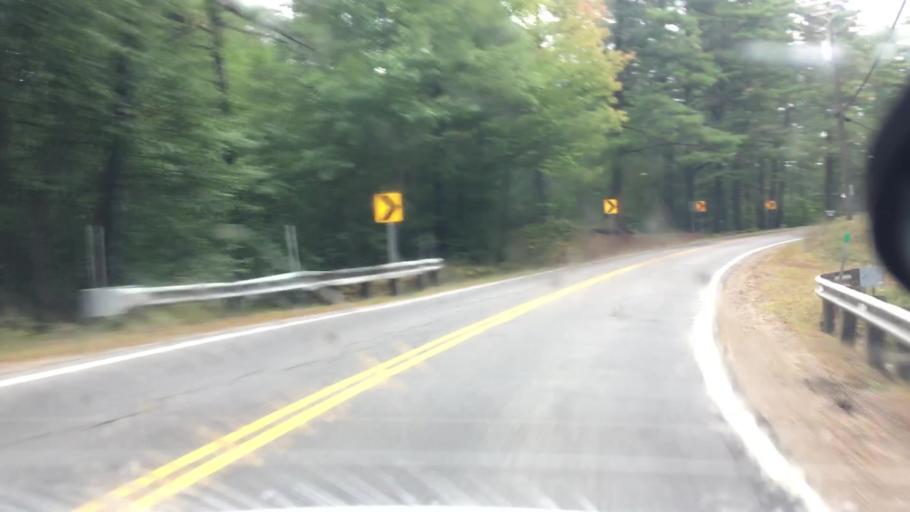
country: US
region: New Hampshire
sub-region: Carroll County
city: Wakefield
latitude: 43.6270
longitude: -70.9880
